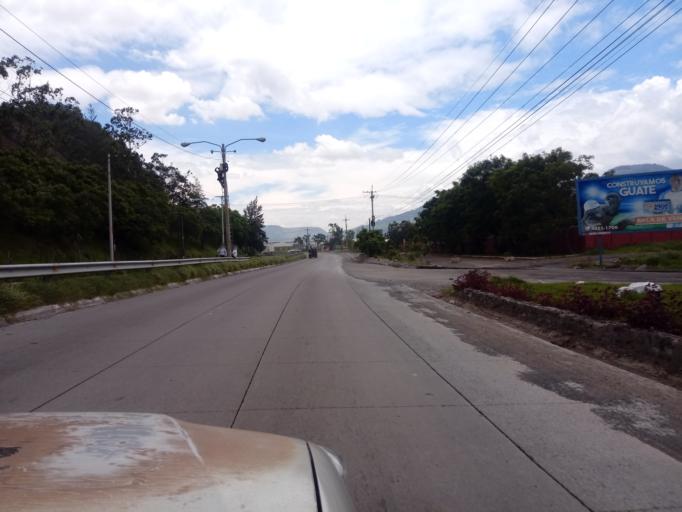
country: GT
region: Escuintla
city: San Vicente Pacaya
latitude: 14.4470
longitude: -90.6457
